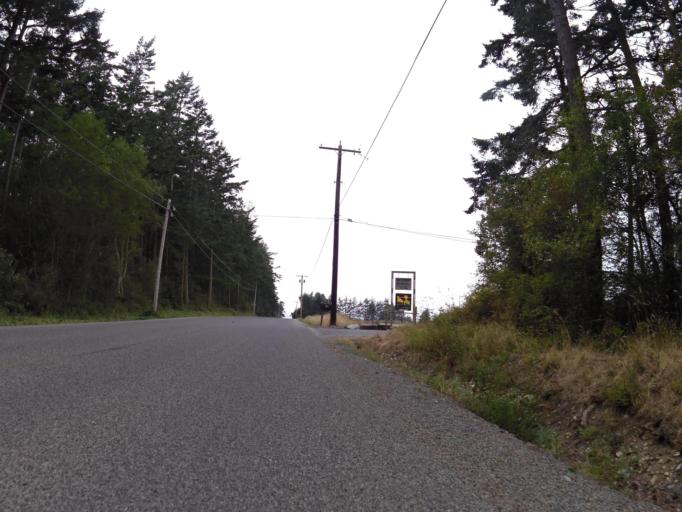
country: US
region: Washington
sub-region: Island County
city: Ault Field
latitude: 48.3007
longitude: -122.7018
